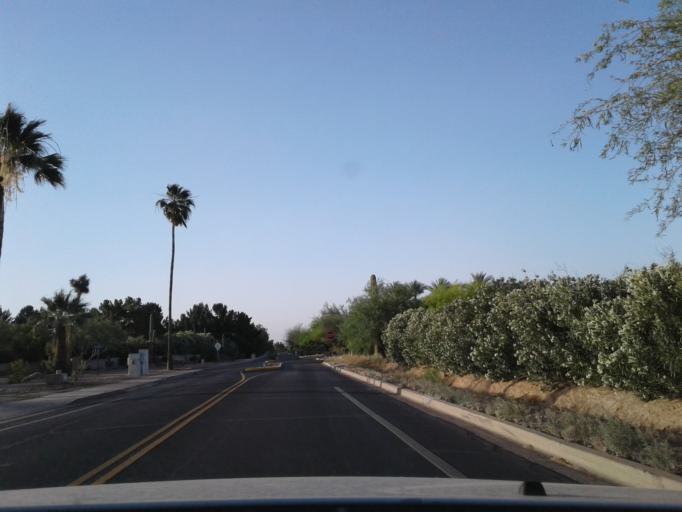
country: US
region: Arizona
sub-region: Maricopa County
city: Paradise Valley
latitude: 33.5675
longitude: -111.9691
